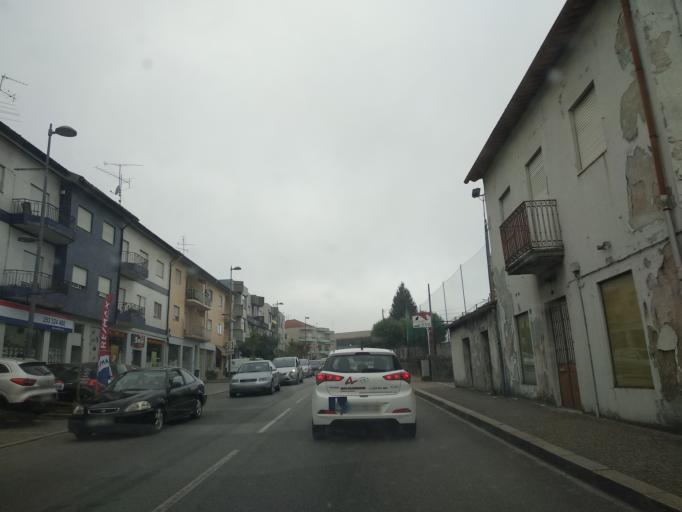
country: PT
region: Braga
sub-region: Vila Verde
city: Vila Verde
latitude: 41.6466
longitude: -8.4361
